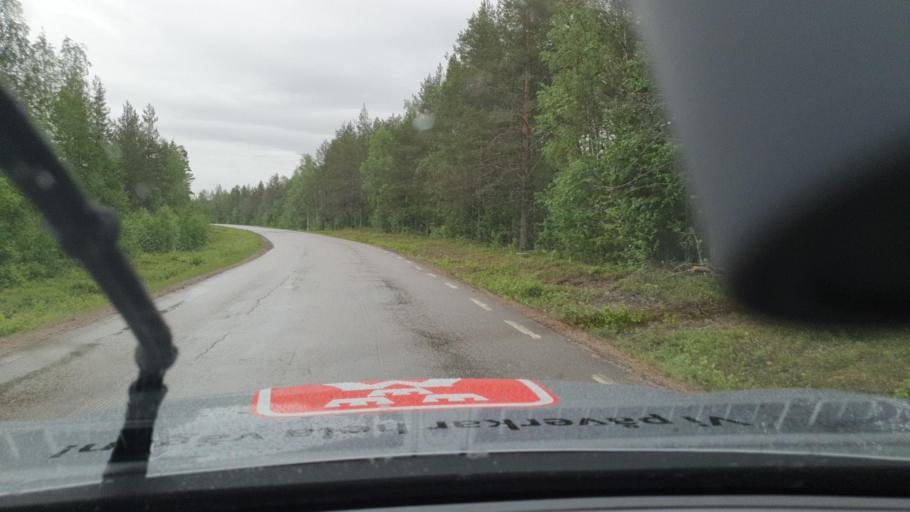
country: SE
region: Norrbotten
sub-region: Pajala Kommun
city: Pajala
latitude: 66.8428
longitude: 23.0736
